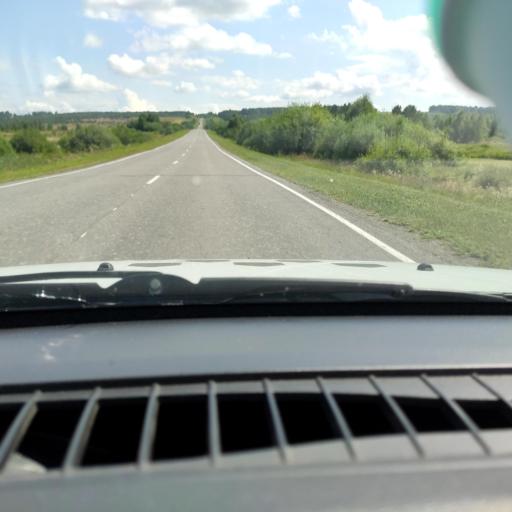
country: RU
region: Chelyabinsk
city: Mezhevoy
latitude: 55.3018
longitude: 58.7476
